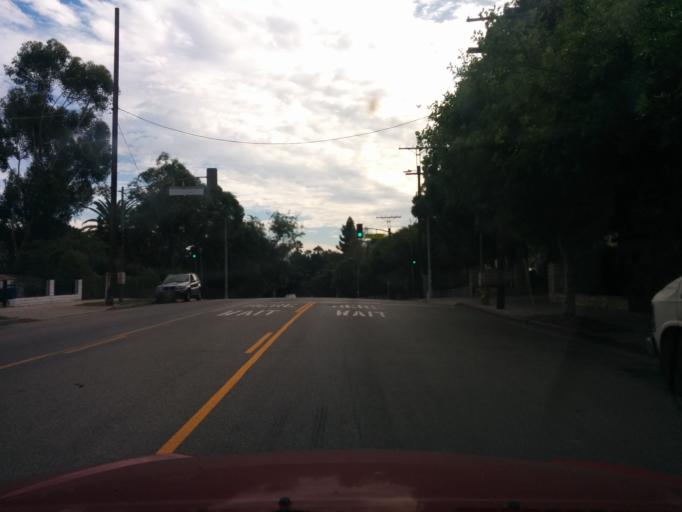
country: US
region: California
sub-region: Los Angeles County
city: Boyle Heights
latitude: 34.0406
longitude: -118.2198
